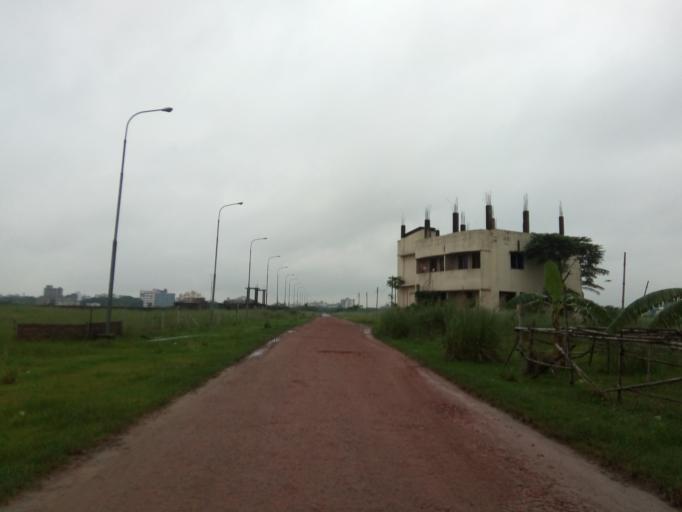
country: BD
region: Dhaka
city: Tungi
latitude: 23.8476
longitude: 90.4330
